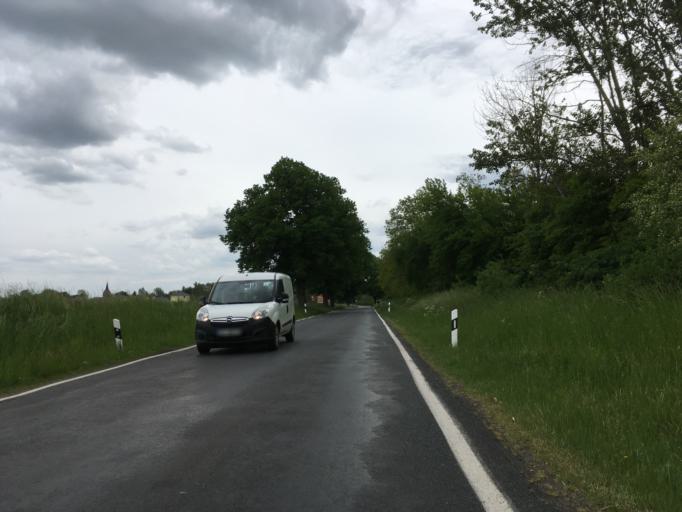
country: DE
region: Brandenburg
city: Werneuchen
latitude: 52.6877
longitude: 13.7284
